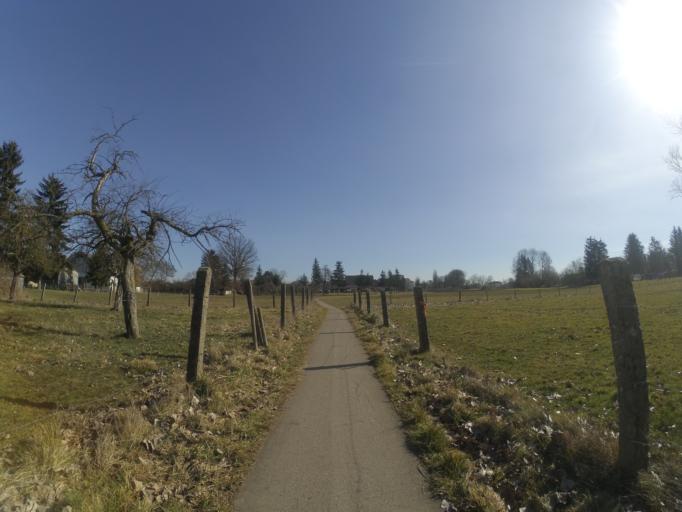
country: DE
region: Baden-Wuerttemberg
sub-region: Tuebingen Region
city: Langenau
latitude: 48.5027
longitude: 10.1355
